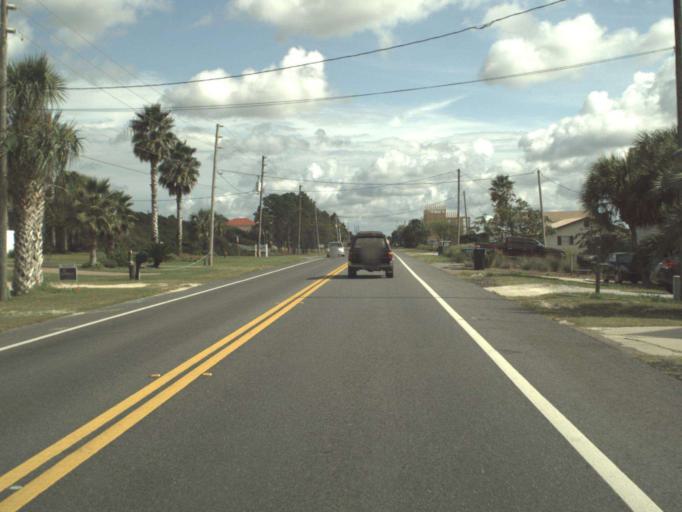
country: US
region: Florida
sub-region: Bay County
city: Mexico Beach
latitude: 29.9185
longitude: -85.3815
